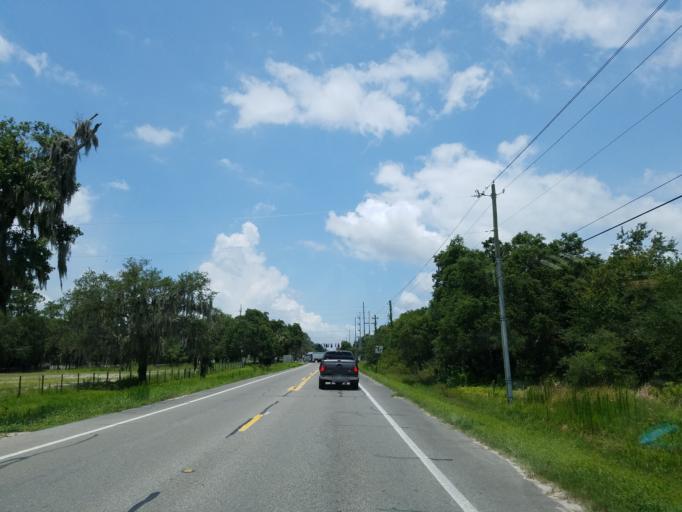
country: US
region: Florida
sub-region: Hillsborough County
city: Fish Hawk
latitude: 27.8504
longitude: -82.1435
